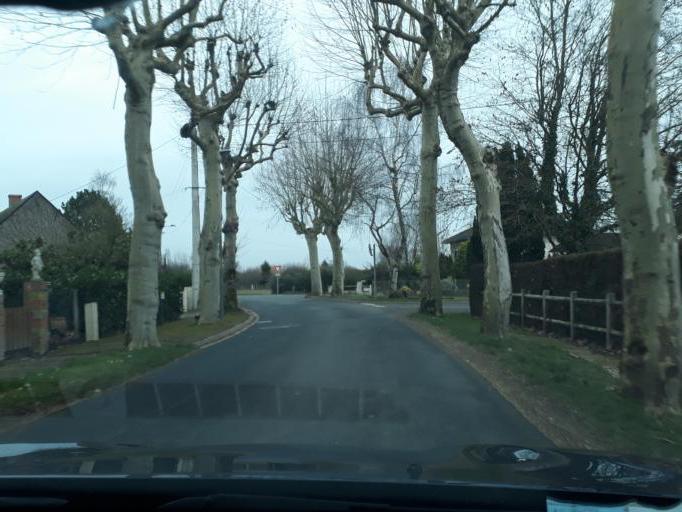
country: FR
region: Centre
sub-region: Departement du Loir-et-Cher
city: Oucques
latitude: 47.8241
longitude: 1.3983
